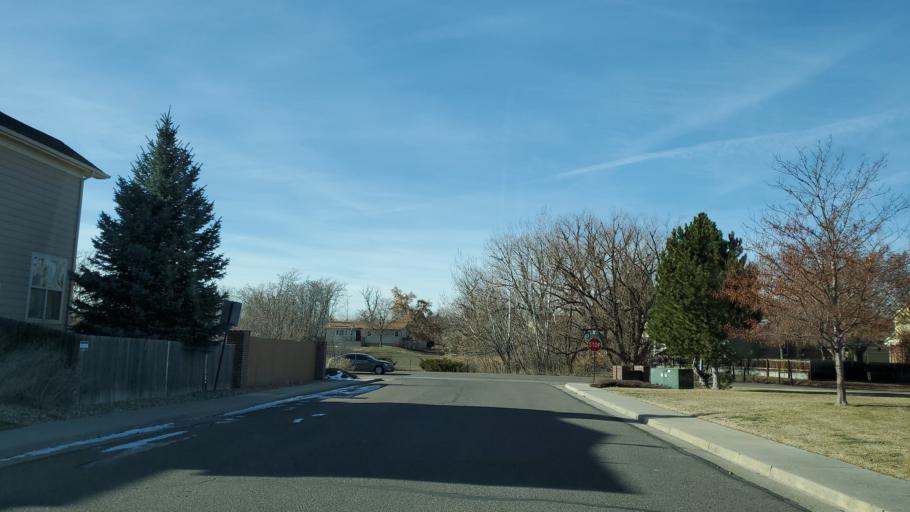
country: US
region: Colorado
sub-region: Adams County
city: Northglenn
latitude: 39.9197
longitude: -104.9490
